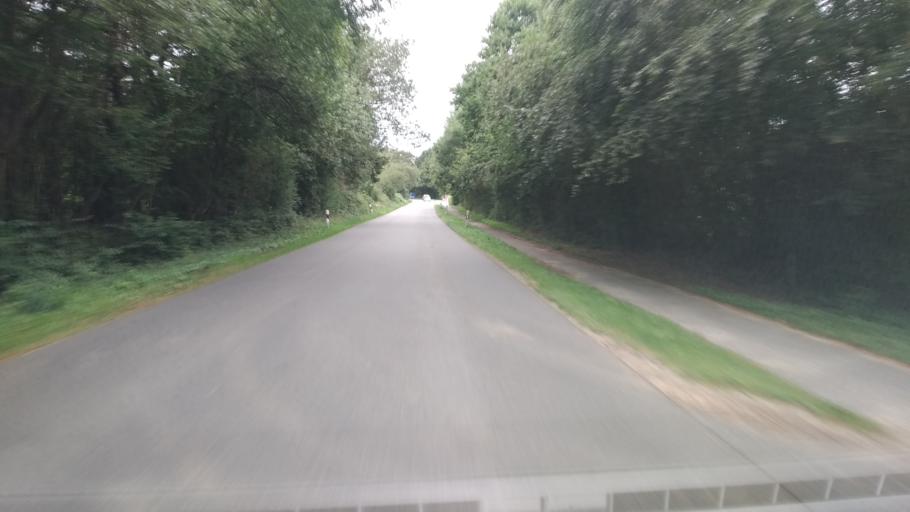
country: DE
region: Schleswig-Holstein
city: Lurschau
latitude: 54.5321
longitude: 9.5142
